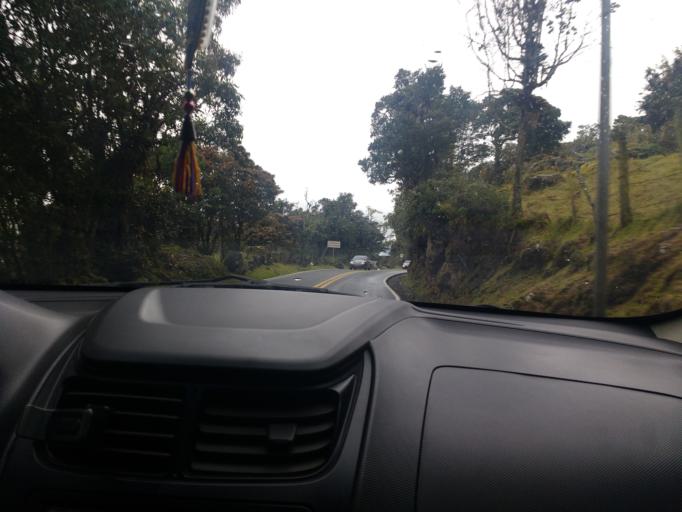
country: CO
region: Cundinamarca
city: Choachi
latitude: 4.5656
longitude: -73.9596
